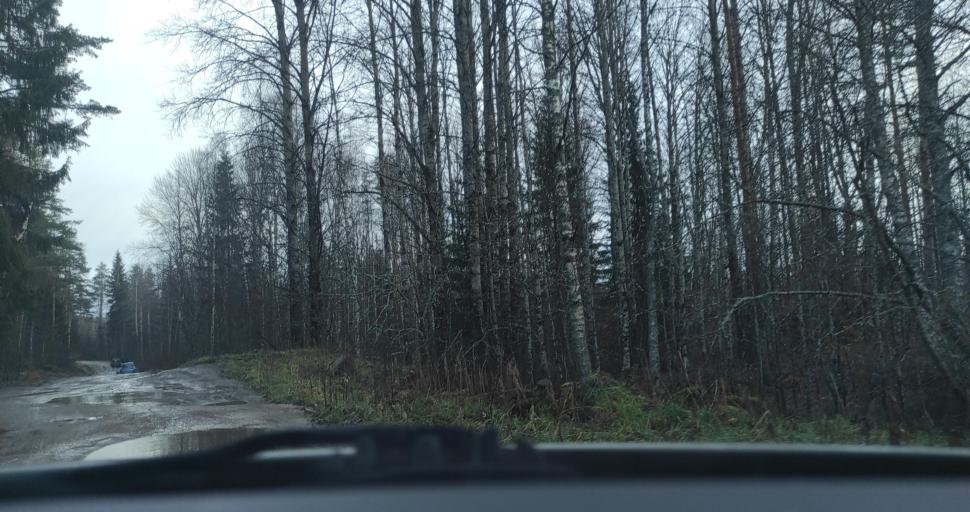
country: RU
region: Republic of Karelia
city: Pitkyaranta
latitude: 61.7433
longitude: 31.3935
